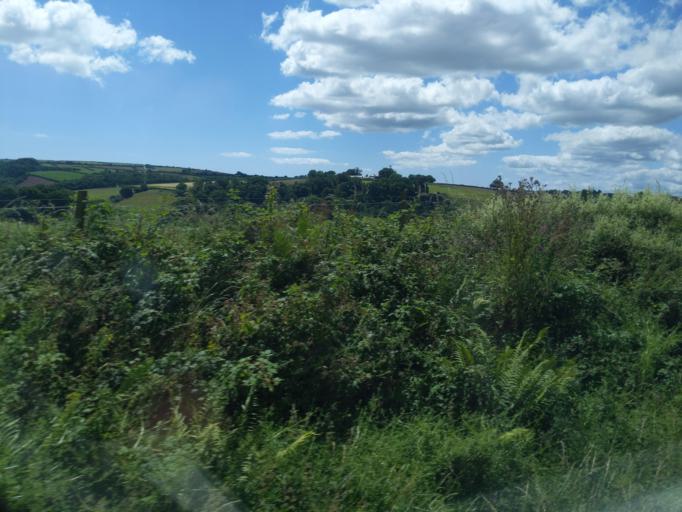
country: GB
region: England
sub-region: Cornwall
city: Liskeard
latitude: 50.4234
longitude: -4.3954
